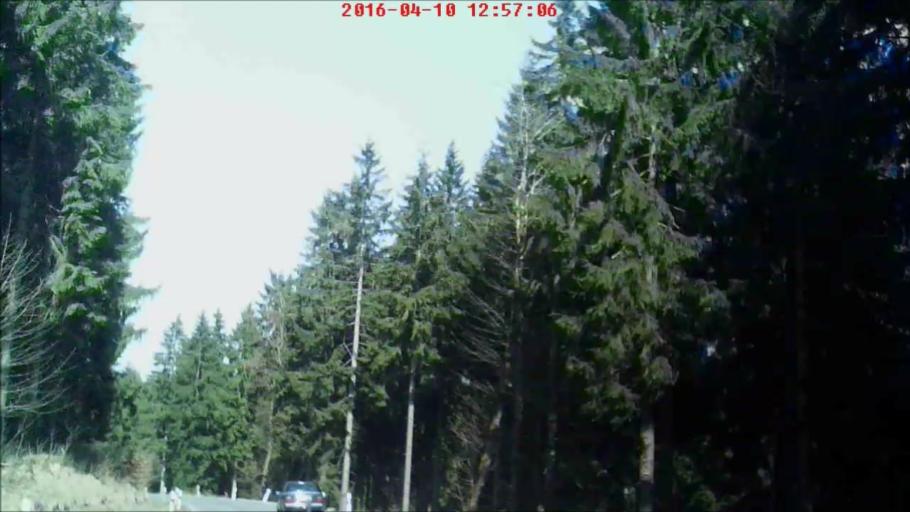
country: DE
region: Thuringia
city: Tabarz
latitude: 50.8333
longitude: 10.5273
